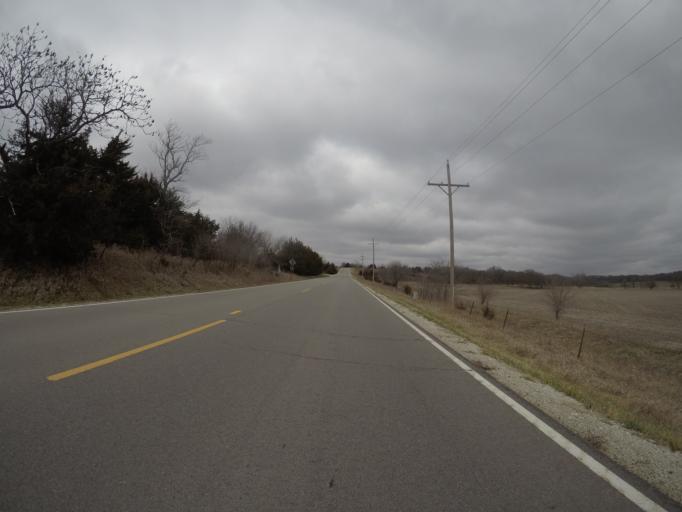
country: US
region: Kansas
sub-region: Pottawatomie County
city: Westmoreland
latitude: 39.4185
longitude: -96.4688
